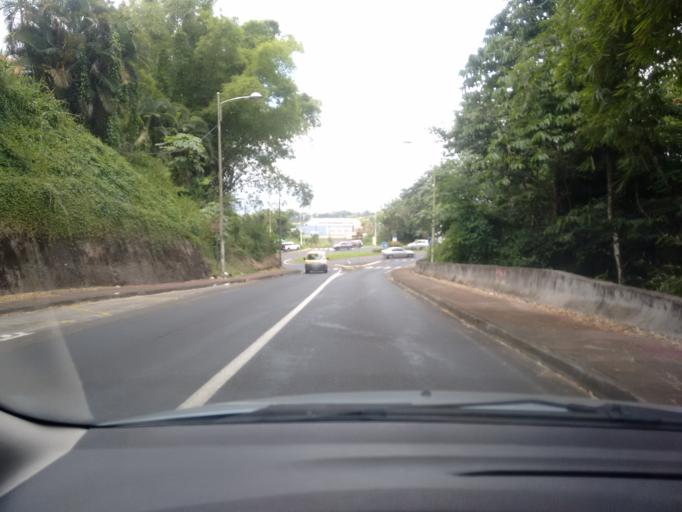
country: MQ
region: Martinique
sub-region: Martinique
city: Saint-Joseph
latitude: 14.6723
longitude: -61.0233
